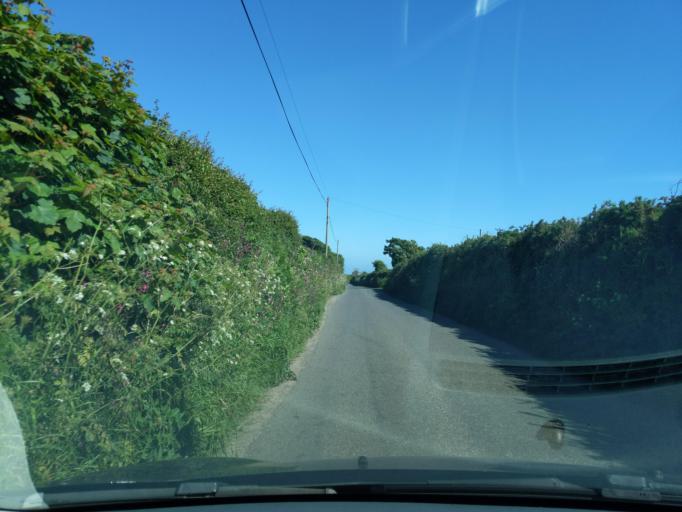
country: GB
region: England
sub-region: Cornwall
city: St. Buryan
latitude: 50.0694
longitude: -5.6101
